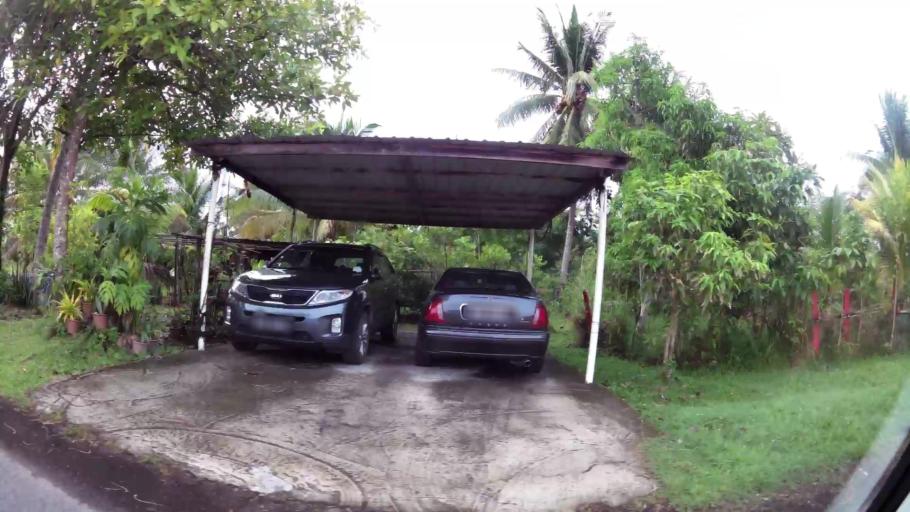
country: BN
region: Belait
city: Seria
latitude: 4.5956
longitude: 114.3256
